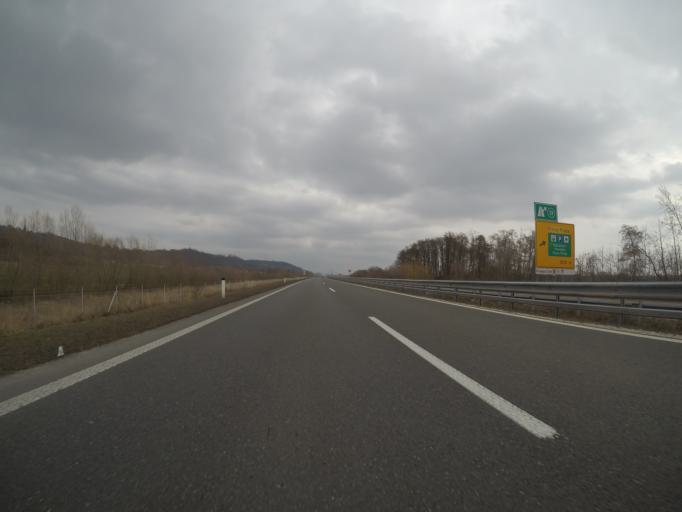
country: HR
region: Medimurska
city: Peklenica
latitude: 46.5255
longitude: 16.5080
